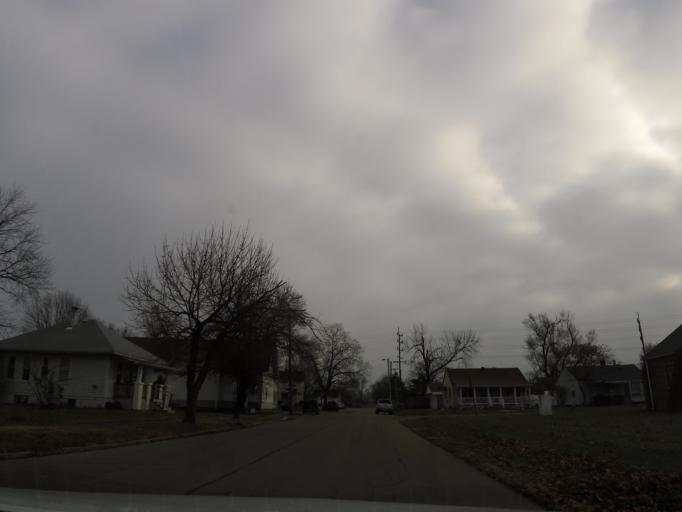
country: US
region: Indiana
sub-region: Bartholomew County
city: Columbus
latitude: 39.2175
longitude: -85.9077
